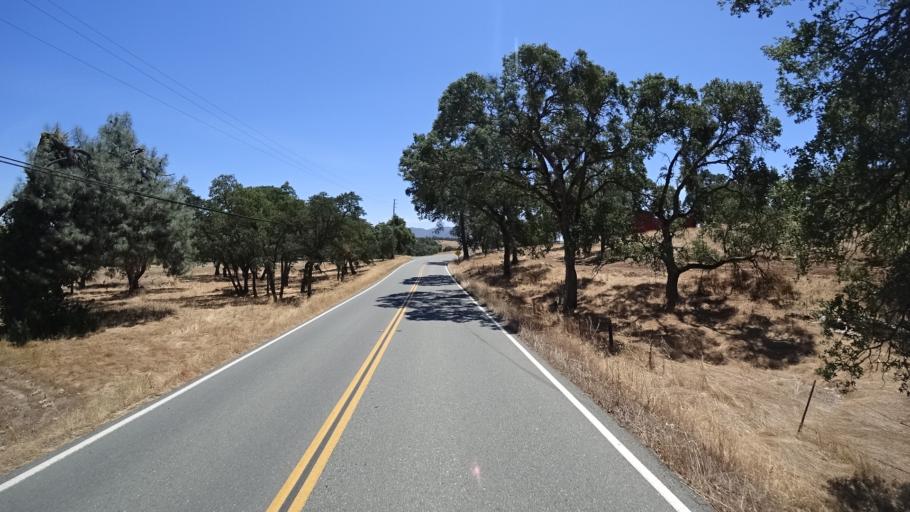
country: US
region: California
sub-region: Calaveras County
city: Valley Springs
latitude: 38.2074
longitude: -120.8282
